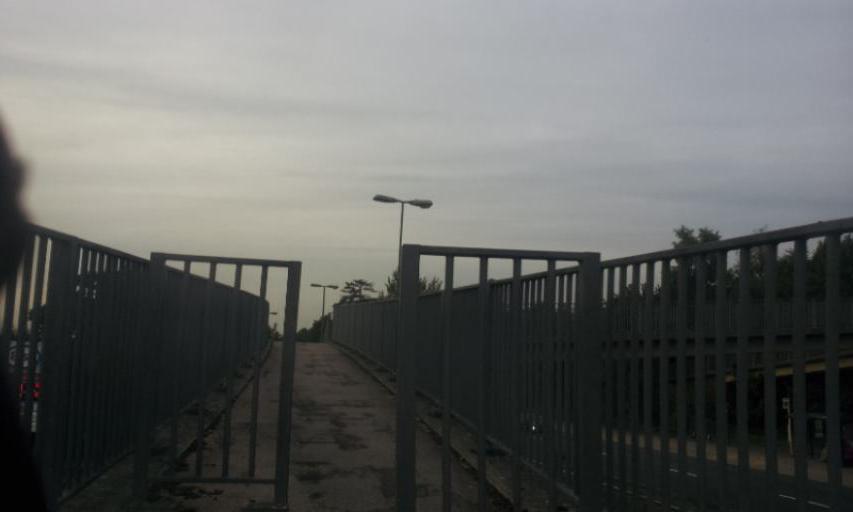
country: GB
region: England
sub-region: Kent
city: Maidstone
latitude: 51.2919
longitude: 0.5175
